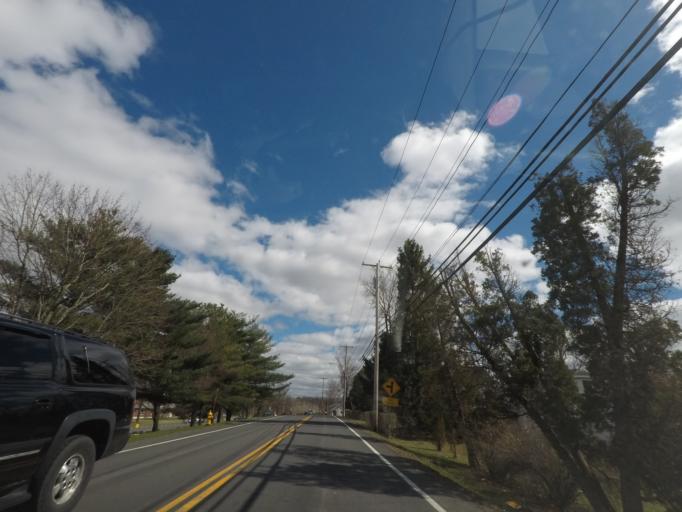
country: US
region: New York
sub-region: Albany County
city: Delmar
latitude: 42.6009
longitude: -73.7902
